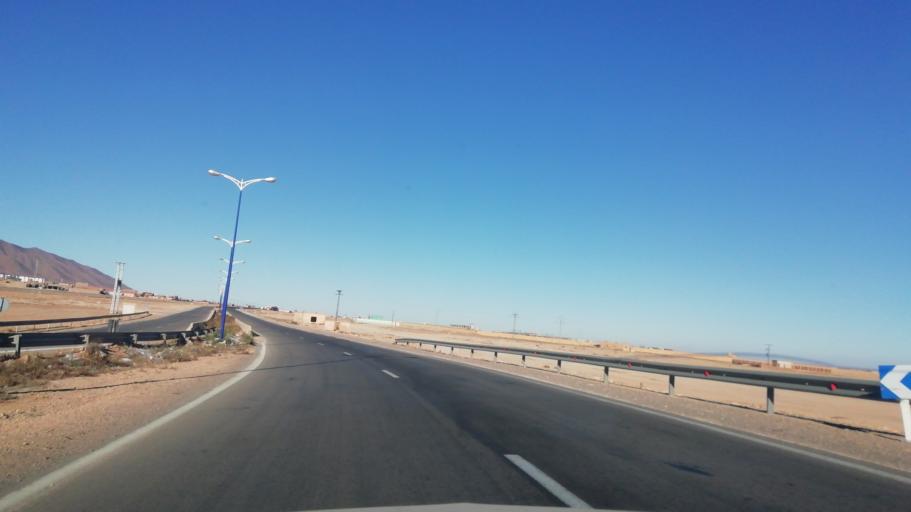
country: DZ
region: Wilaya de Naama
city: Naama
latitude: 33.5142
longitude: -0.2776
